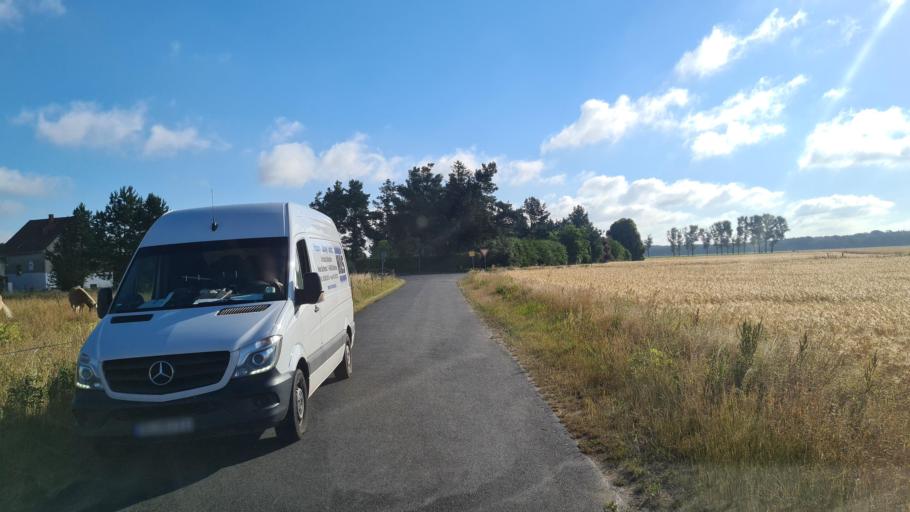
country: DE
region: Saxony
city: Beilrode
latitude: 51.6328
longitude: 13.1198
